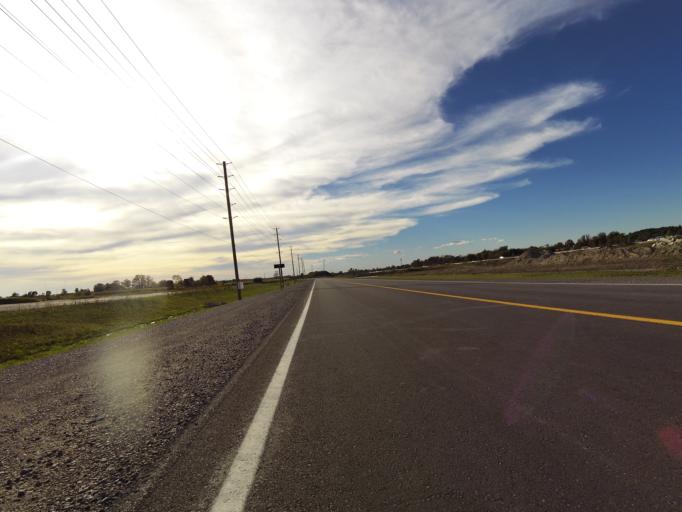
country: CA
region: Ontario
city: Oshawa
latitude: 43.8788
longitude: -78.7532
